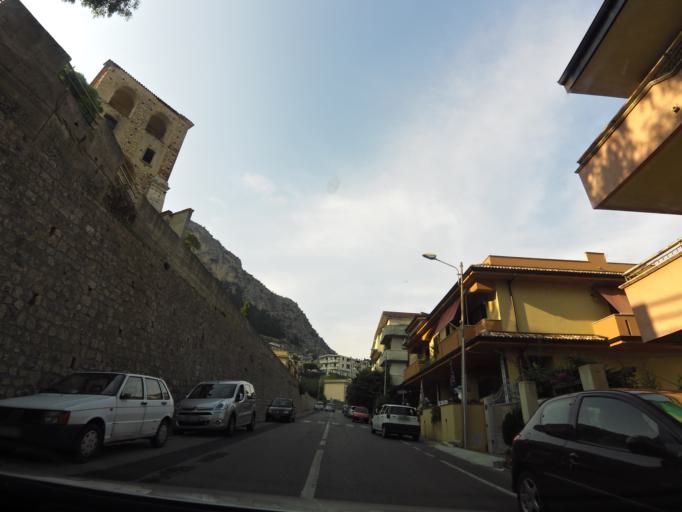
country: IT
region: Calabria
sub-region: Provincia di Reggio Calabria
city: Stilo
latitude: 38.4750
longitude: 16.4668
